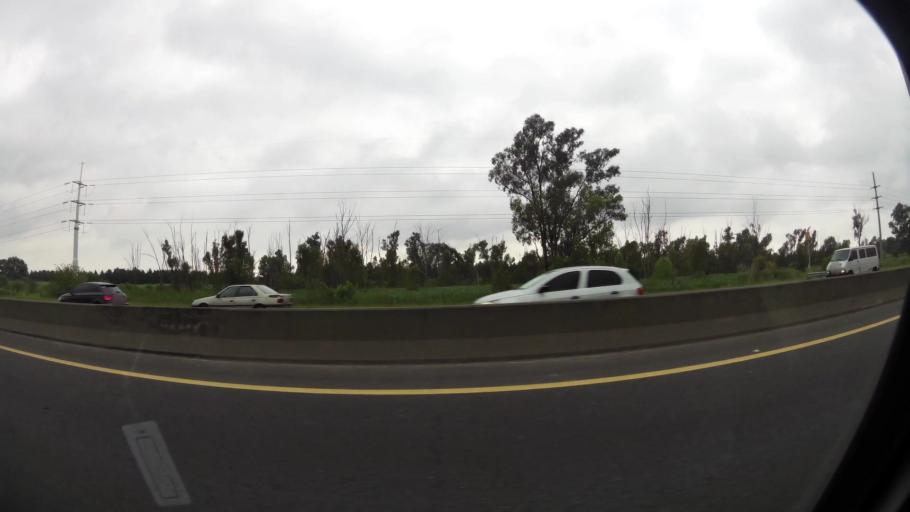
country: AR
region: Buenos Aires
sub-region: Partido de Quilmes
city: Quilmes
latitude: -34.6933
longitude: -58.2827
